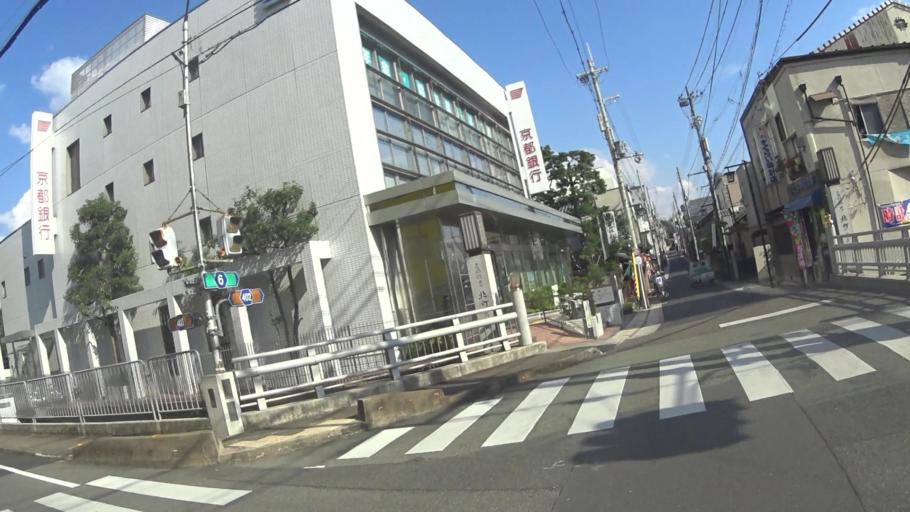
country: JP
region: Kyoto
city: Kameoka
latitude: 35.0159
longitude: 135.5761
